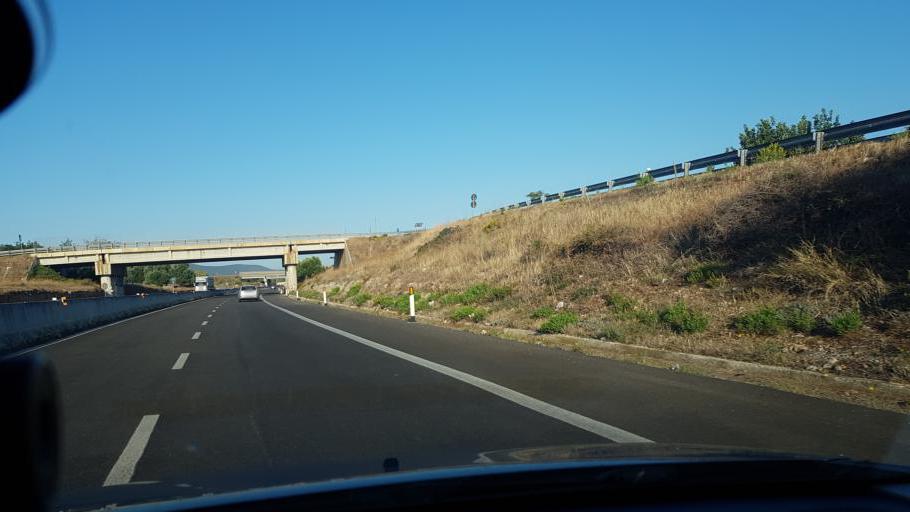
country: IT
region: Apulia
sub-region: Provincia di Brindisi
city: Pezze di Greco
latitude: 40.8345
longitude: 17.3922
